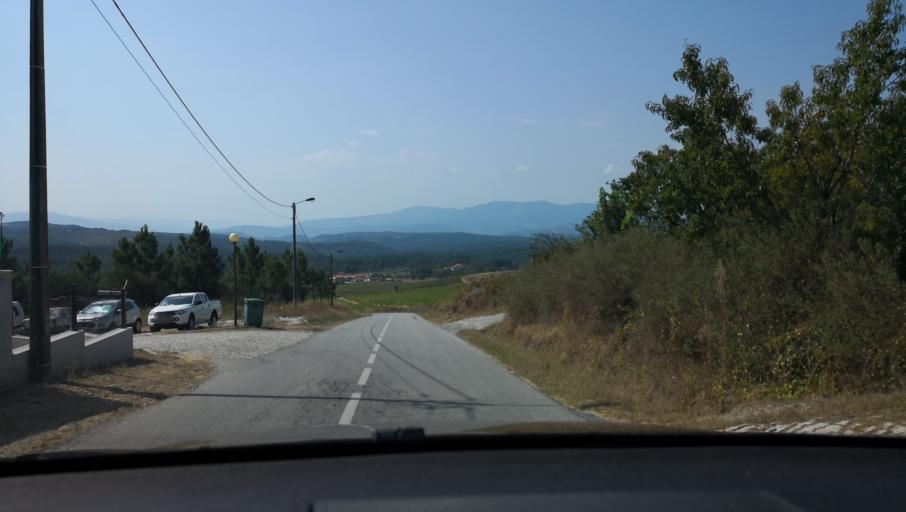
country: PT
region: Vila Real
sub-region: Sabrosa
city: Sabrosa
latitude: 41.2718
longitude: -7.6201
